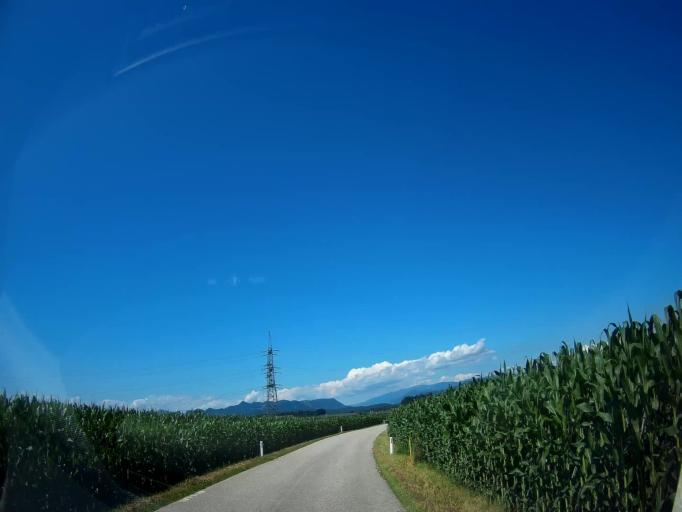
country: AT
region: Carinthia
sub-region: Politischer Bezirk Klagenfurt Land
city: Grafenstein
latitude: 46.6163
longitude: 14.4519
